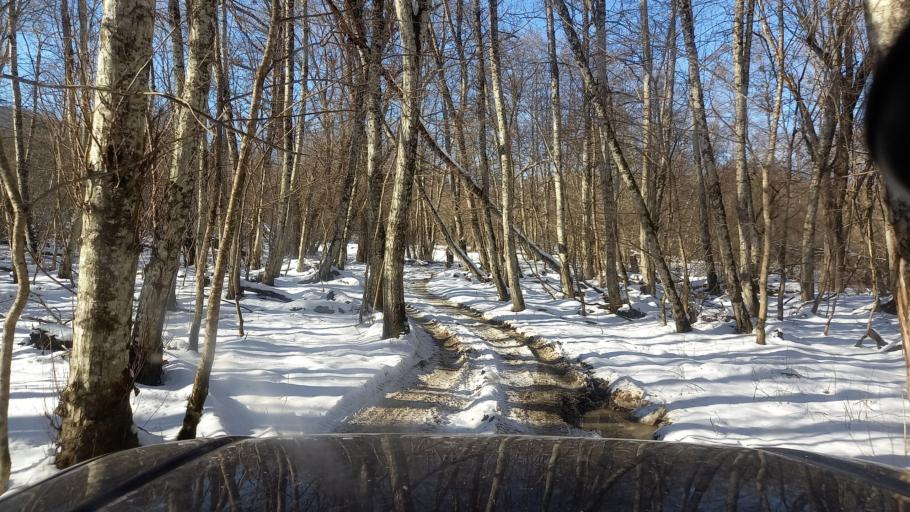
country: RU
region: Adygeya
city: Kamennomostskiy
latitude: 44.2067
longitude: 40.1475
